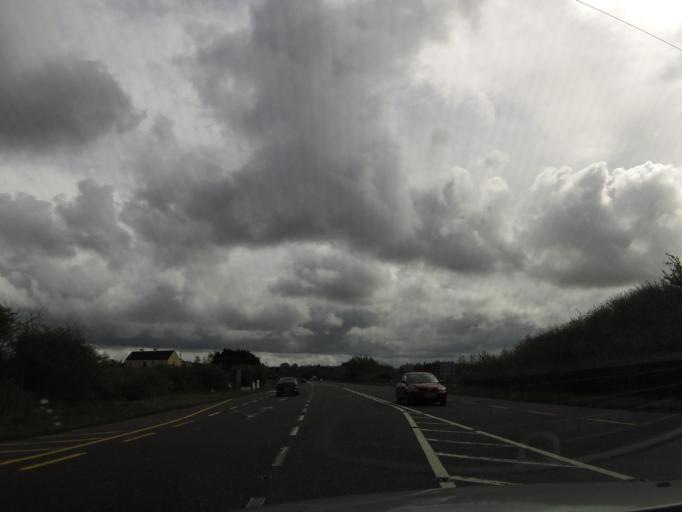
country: IE
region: Connaught
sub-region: Maigh Eo
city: Claremorris
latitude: 53.7093
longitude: -8.9846
